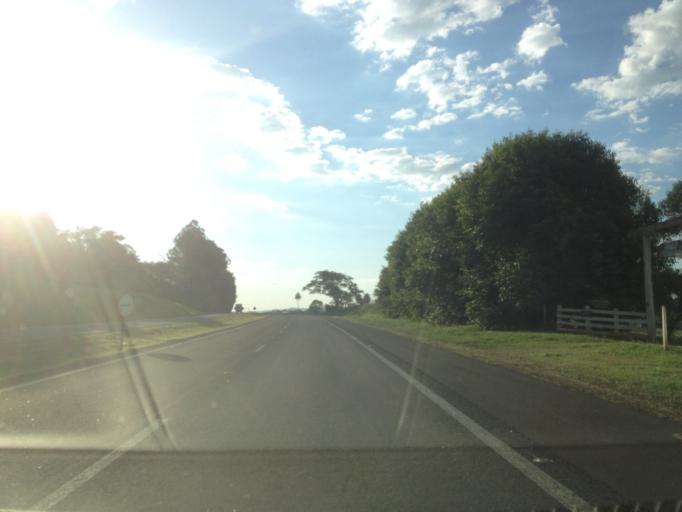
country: BR
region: Sao Paulo
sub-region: Brotas
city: Brotas
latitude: -22.2513
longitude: -48.2485
